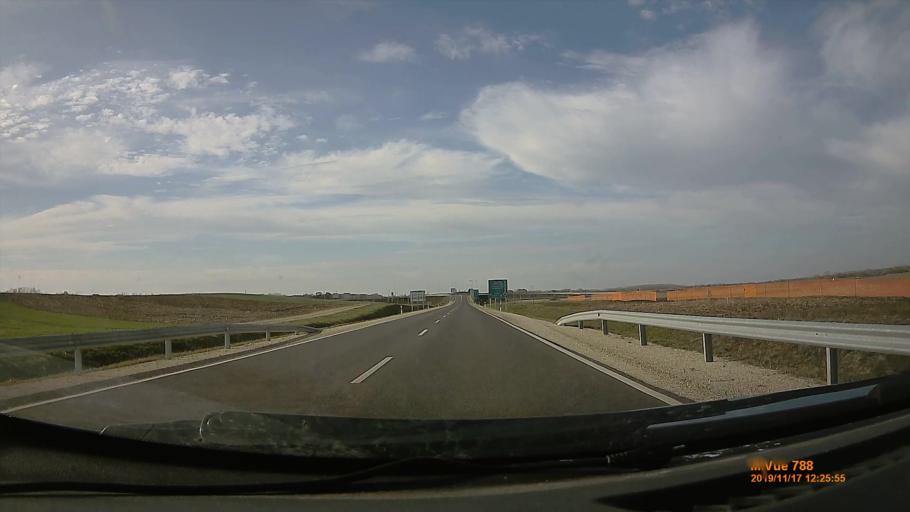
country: HU
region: Bacs-Kiskun
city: Kecskemet
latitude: 46.9319
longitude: 19.6254
